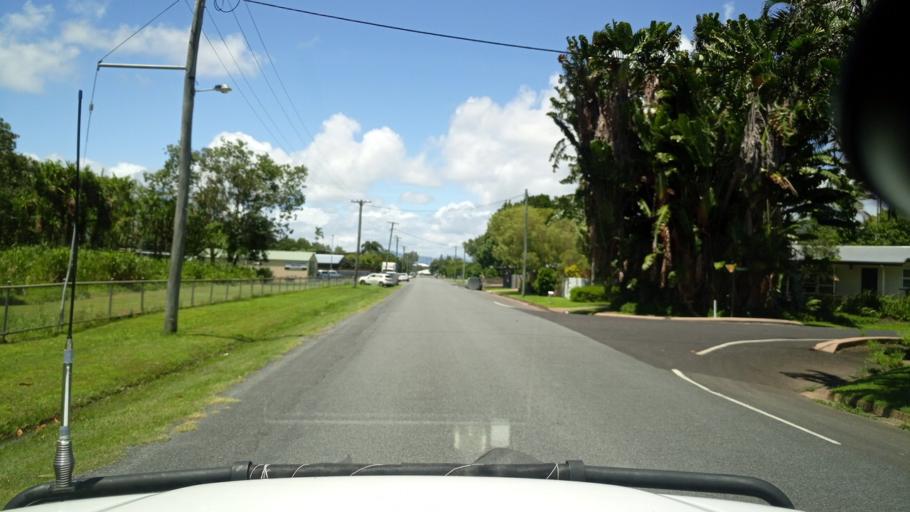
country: AU
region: Queensland
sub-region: Cairns
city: Cairns
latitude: -16.9202
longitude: 145.7501
